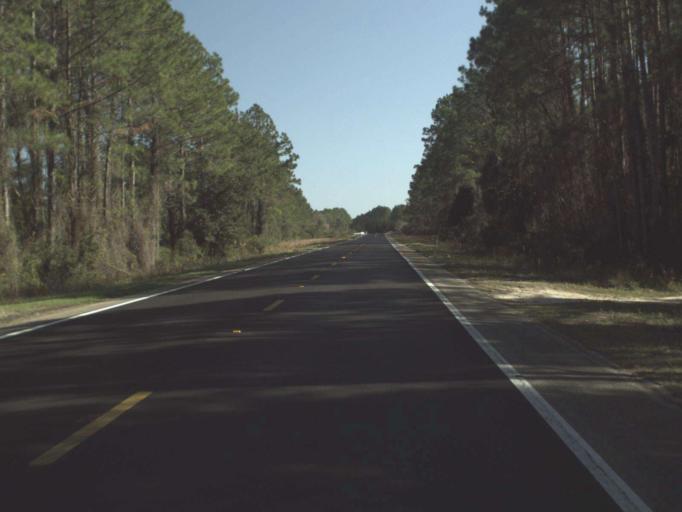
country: US
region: Florida
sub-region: Gulf County
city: Port Saint Joe
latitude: 29.7523
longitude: -85.2479
